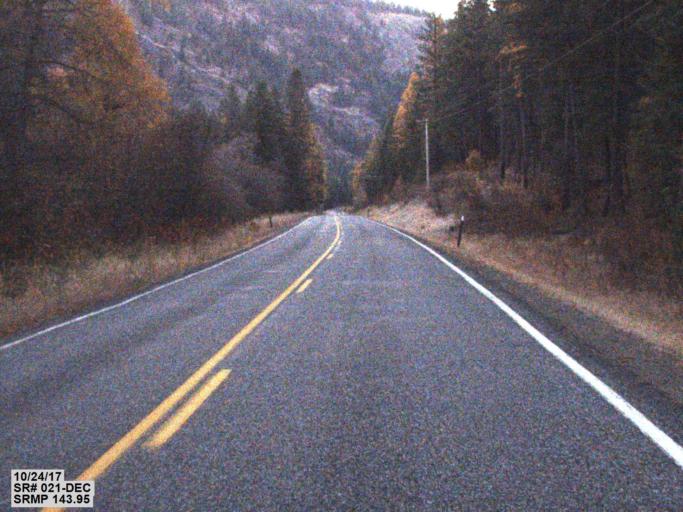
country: US
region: Washington
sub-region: Ferry County
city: Republic
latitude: 48.4364
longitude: -118.7370
